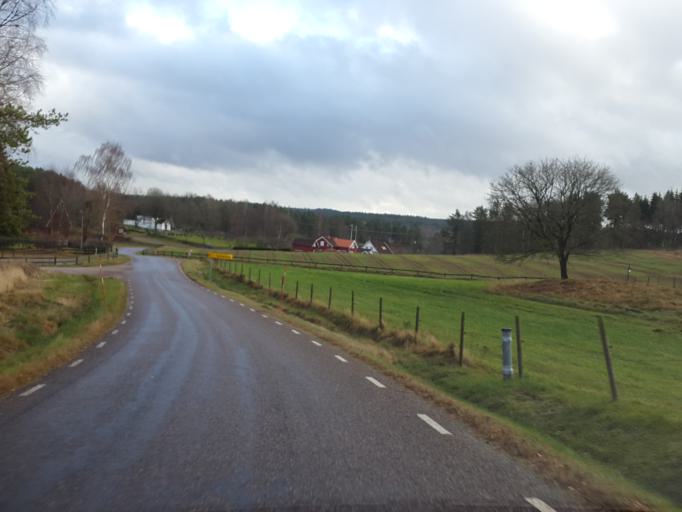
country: SE
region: Vaestra Goetaland
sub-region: Vargarda Kommun
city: Jonstorp
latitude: 57.9959
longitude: 12.7662
